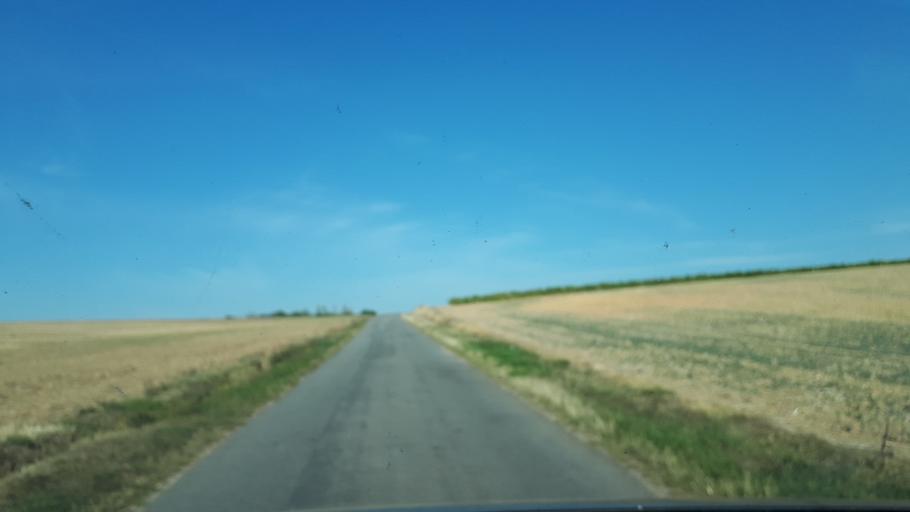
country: FR
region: Centre
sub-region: Departement du Loir-et-Cher
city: Villiers-sur-Loir
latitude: 47.8267
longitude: 0.9664
